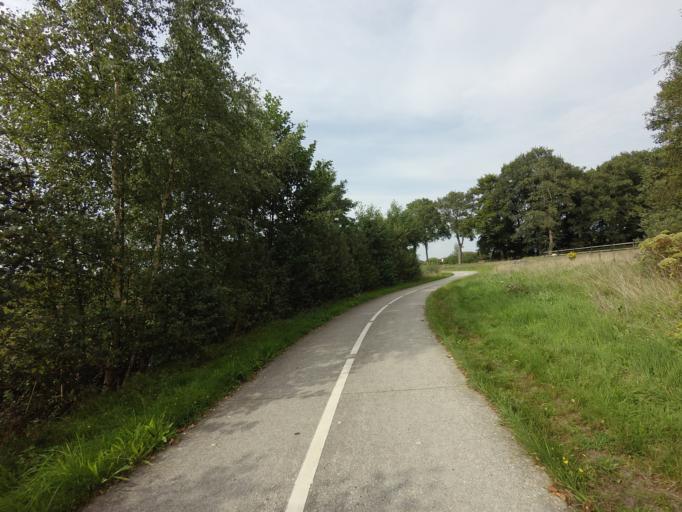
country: NL
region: Drenthe
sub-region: Gemeente Westerveld
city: Dwingeloo
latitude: 52.9071
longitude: 6.2862
